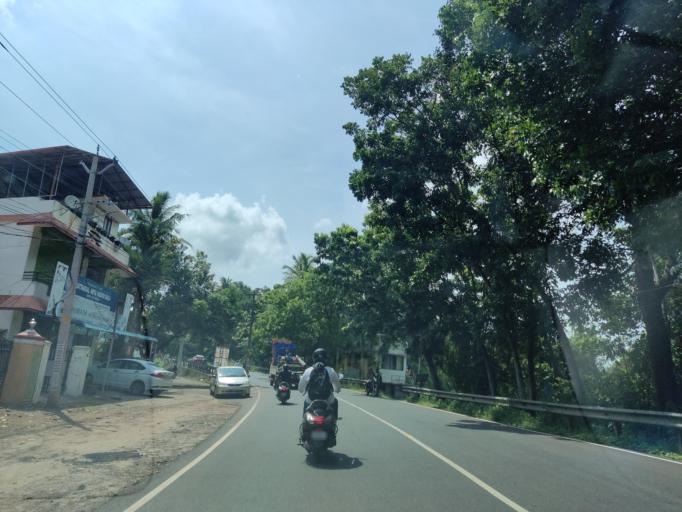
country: IN
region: Kerala
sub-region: Alappuzha
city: Mavelikara
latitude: 9.2616
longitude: 76.5439
